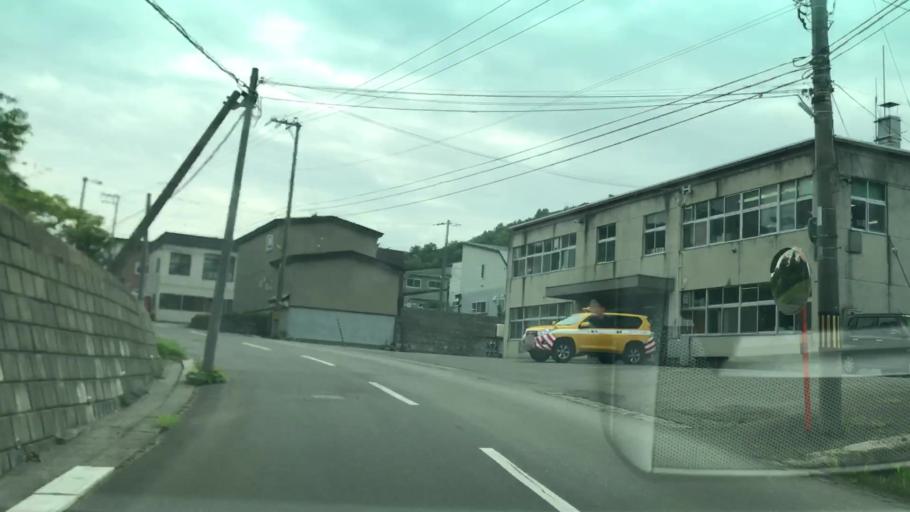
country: JP
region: Hokkaido
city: Otaru
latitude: 43.2108
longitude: 140.9370
